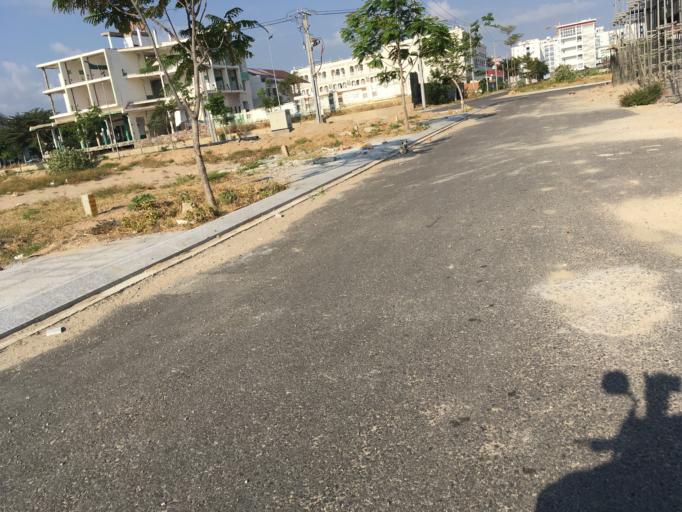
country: VN
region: Ninh Thuan
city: Phan Rang-Thap Cham
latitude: 11.5639
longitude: 109.0207
